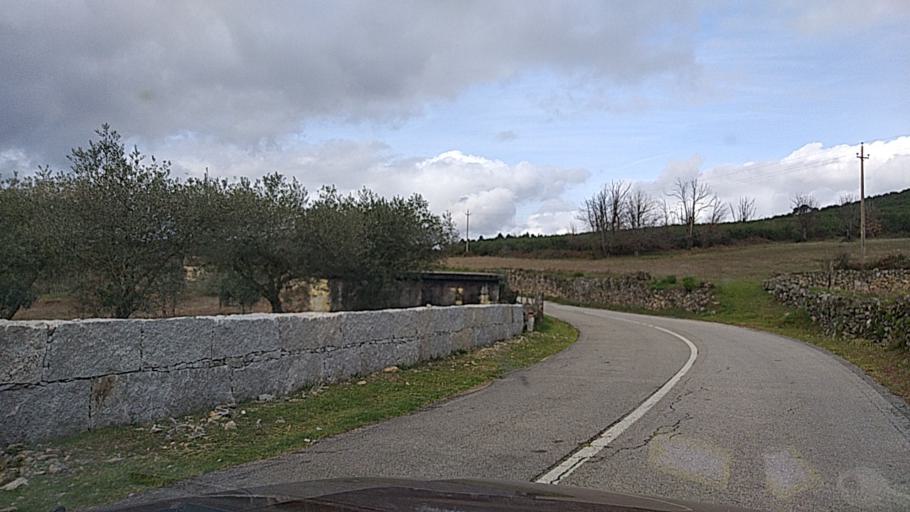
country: PT
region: Guarda
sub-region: Fornos de Algodres
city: Fornos de Algodres
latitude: 40.6582
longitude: -7.5865
